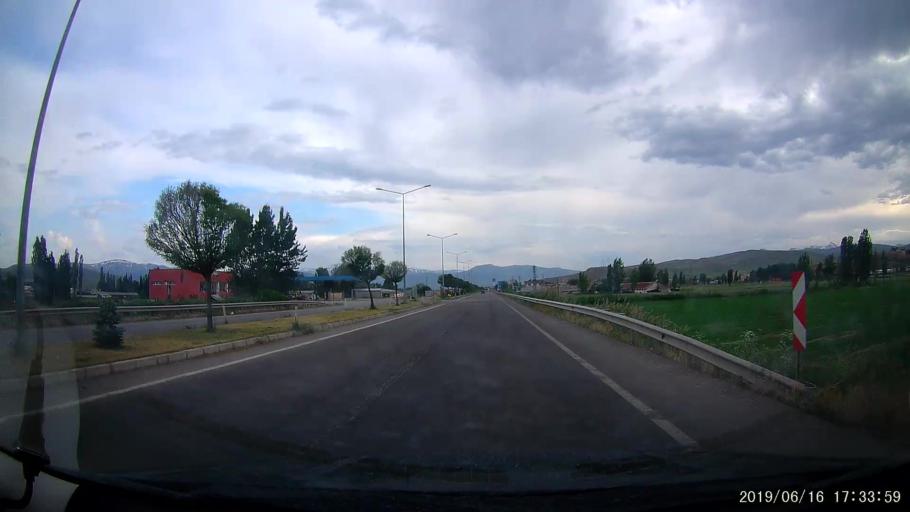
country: TR
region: Erzincan
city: Tercan
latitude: 39.7460
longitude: 40.2737
